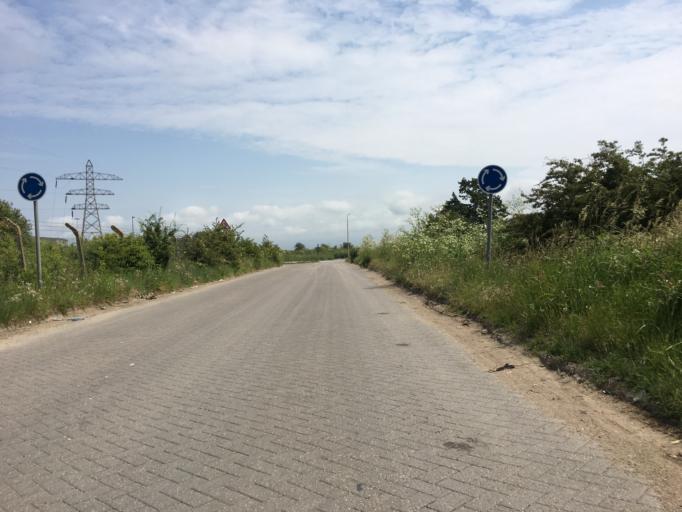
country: GB
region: England
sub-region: Kent
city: Queenborough
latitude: 51.3796
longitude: 0.7563
